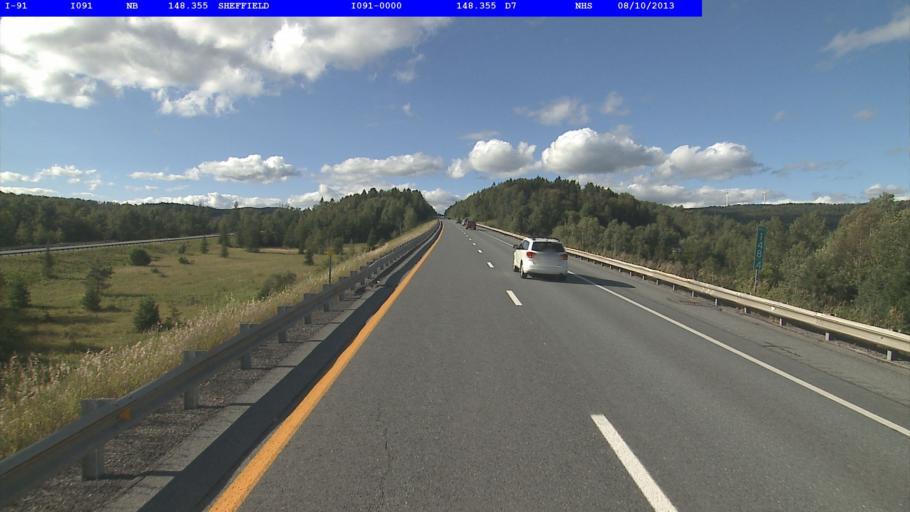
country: US
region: Vermont
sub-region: Caledonia County
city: Lyndonville
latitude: 44.6409
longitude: -72.1306
